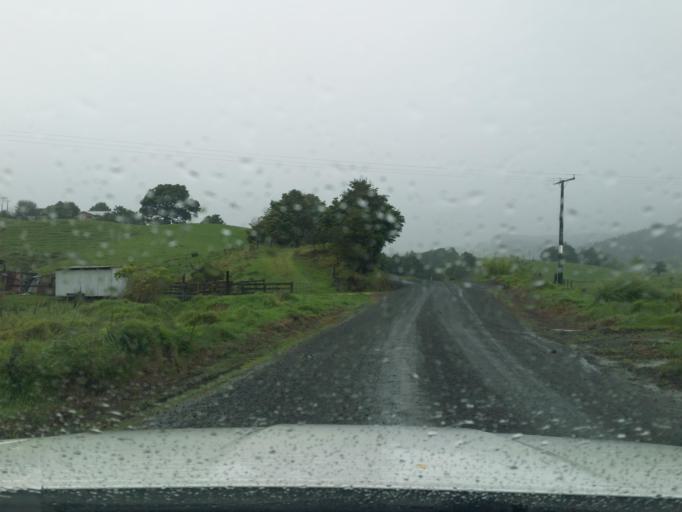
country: NZ
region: Northland
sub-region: Kaipara District
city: Dargaville
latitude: -35.7762
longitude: 173.9588
